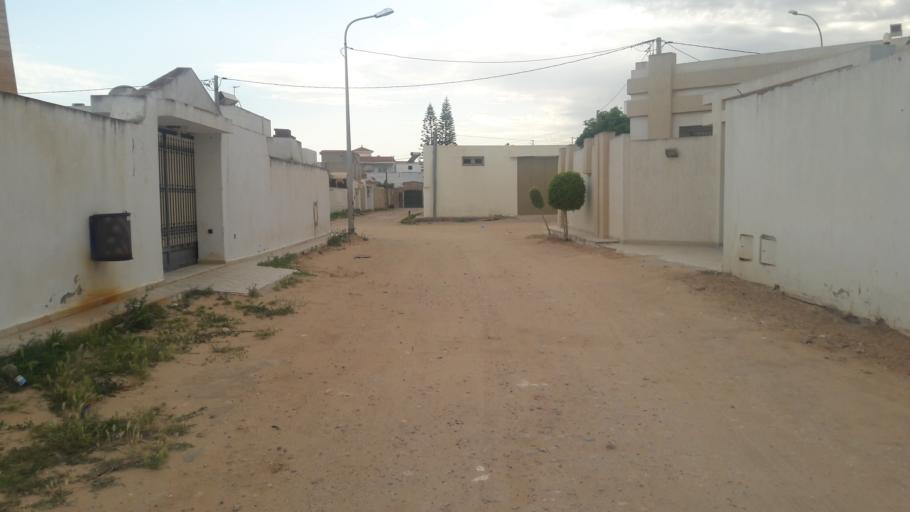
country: TN
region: Safaqis
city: Al Qarmadah
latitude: 34.8114
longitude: 10.7458
